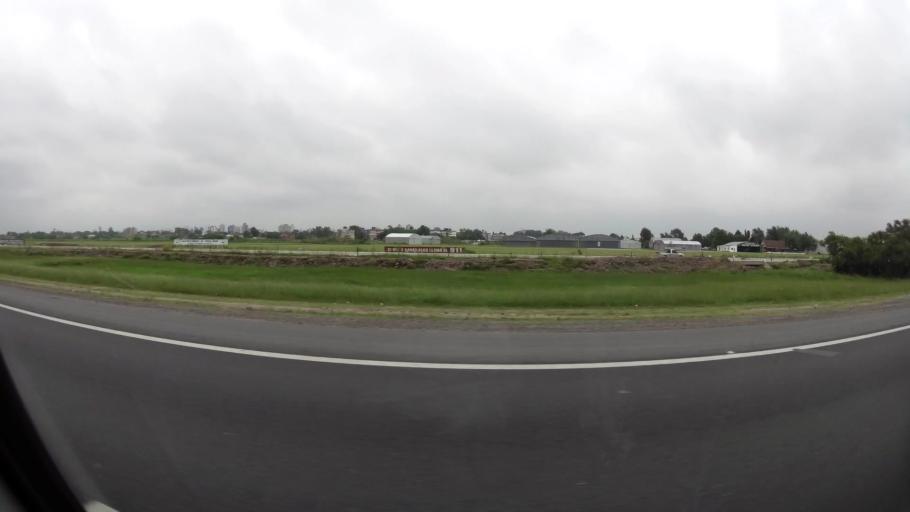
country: AR
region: Buenos Aires
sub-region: Partido de Quilmes
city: Quilmes
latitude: -34.7439
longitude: -58.2034
